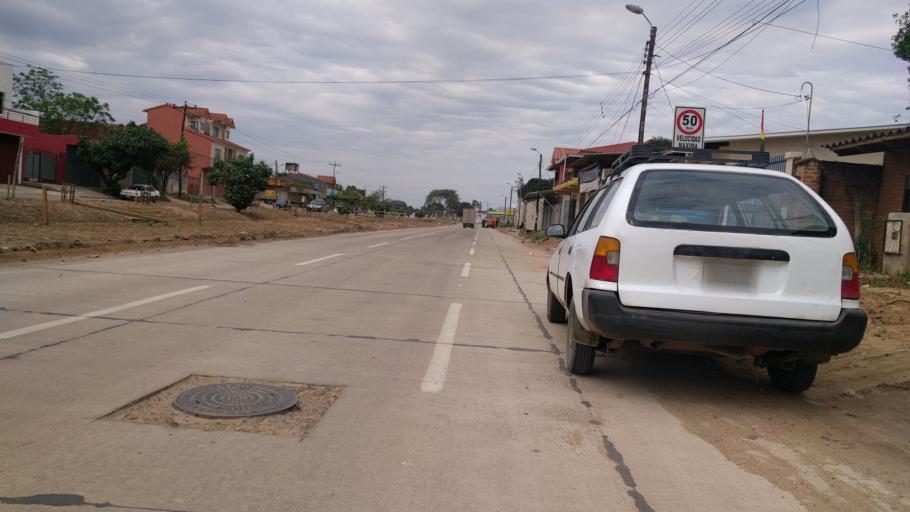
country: BO
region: Santa Cruz
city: Santa Cruz de la Sierra
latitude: -17.8343
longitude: -63.1751
